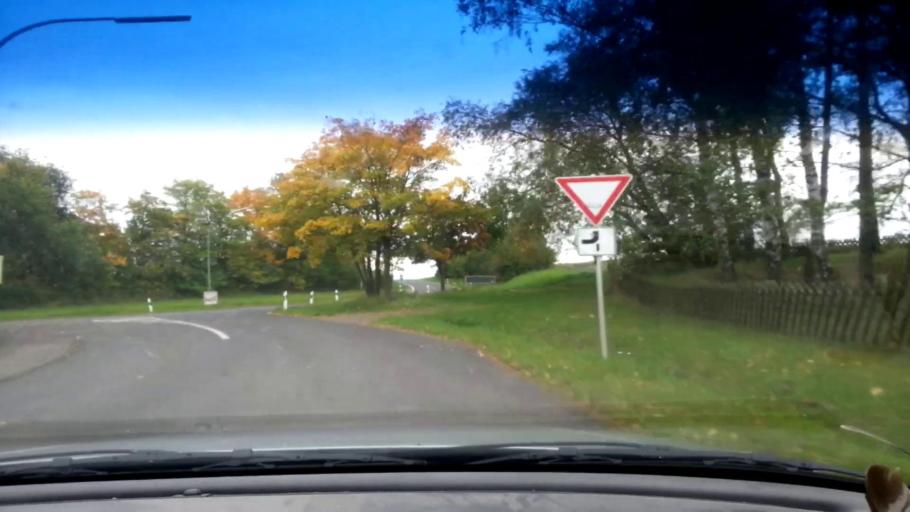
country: DE
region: Bavaria
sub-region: Upper Franconia
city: Gerach
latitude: 50.0281
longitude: 10.8102
